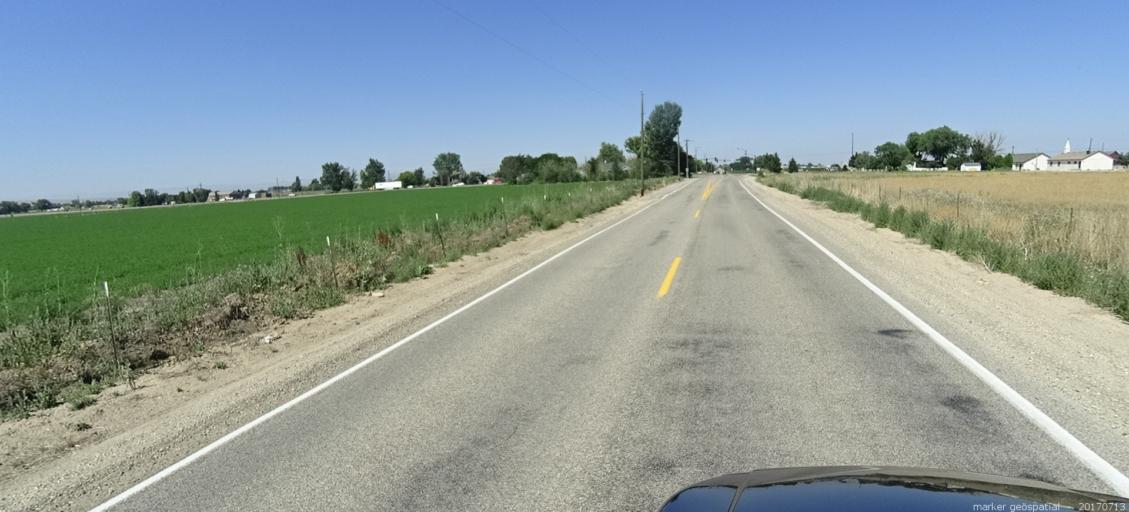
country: US
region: Idaho
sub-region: Ada County
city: Kuna
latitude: 43.5319
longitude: -116.3907
